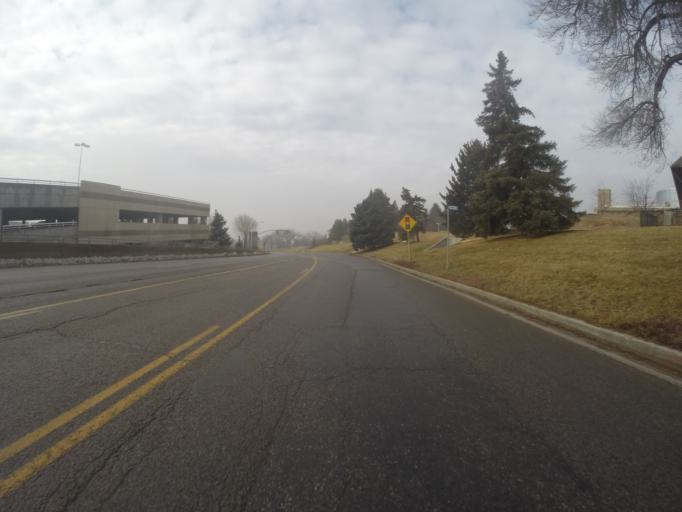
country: US
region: Utah
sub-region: Salt Lake County
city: Salt Lake City
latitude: 40.7728
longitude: -111.8393
